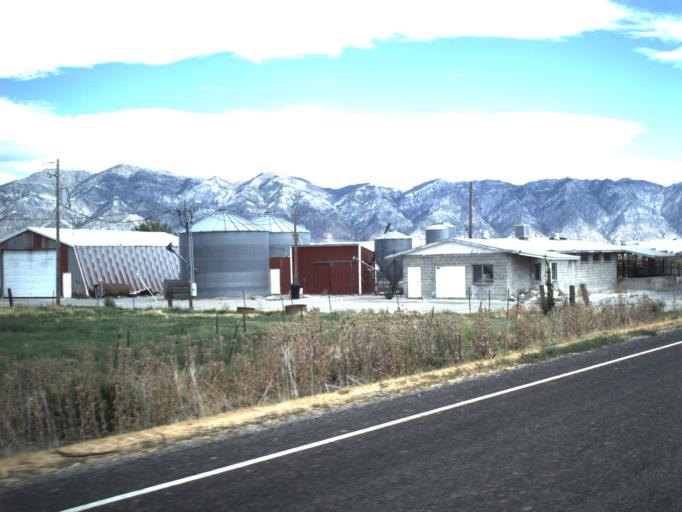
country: US
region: Utah
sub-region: Box Elder County
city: Honeyville
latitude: 41.5608
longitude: -112.1565
